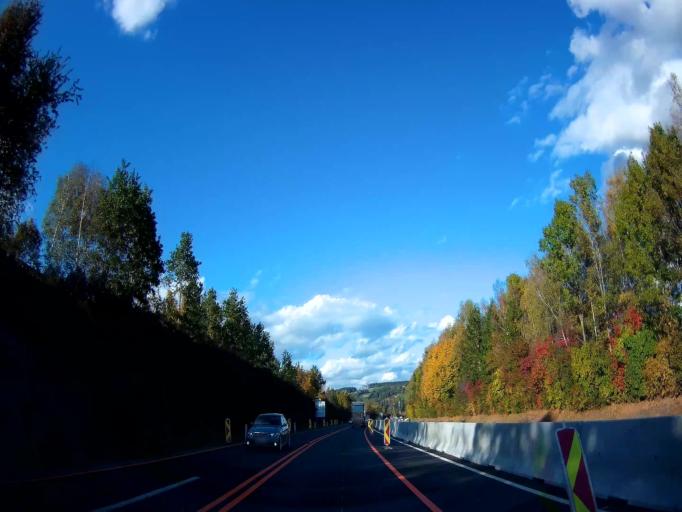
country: AT
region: Carinthia
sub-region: Politischer Bezirk Wolfsberg
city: Wolfsberg
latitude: 46.8304
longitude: 14.8181
